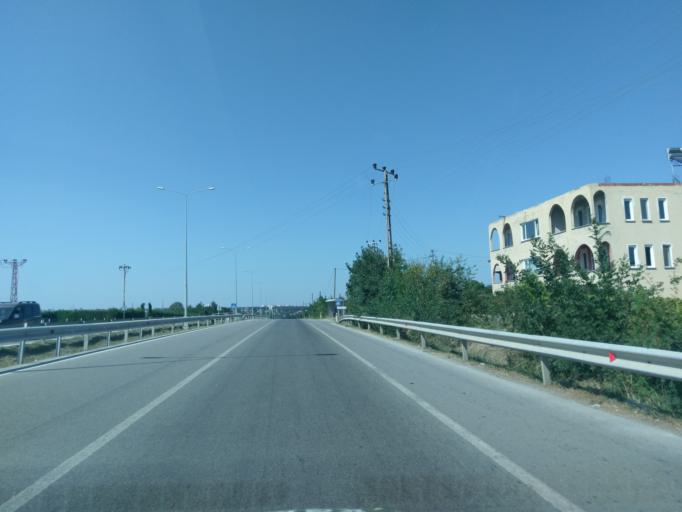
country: TR
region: Samsun
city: Bafra
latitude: 41.5303
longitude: 35.9518
